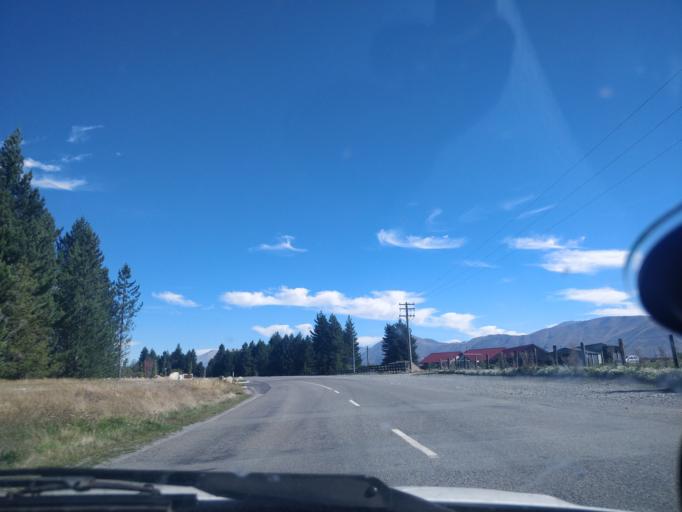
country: NZ
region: Otago
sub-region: Queenstown-Lakes District
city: Wanaka
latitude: -44.2650
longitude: 170.0813
